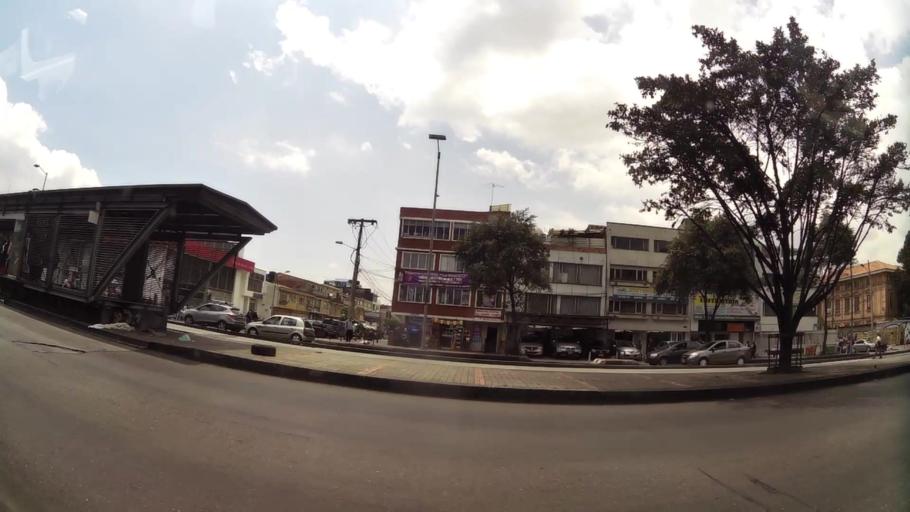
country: CO
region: Bogota D.C.
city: Bogota
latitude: 4.5867
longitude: -74.0935
